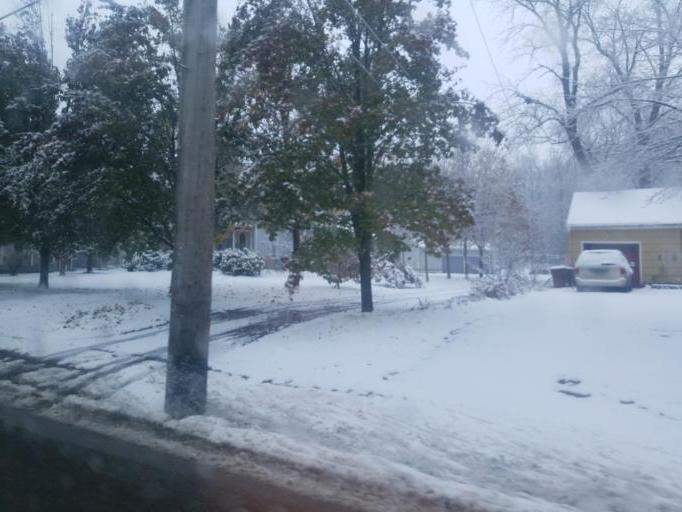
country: US
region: Ohio
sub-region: Geauga County
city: Middlefield
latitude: 41.4584
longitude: -81.0754
